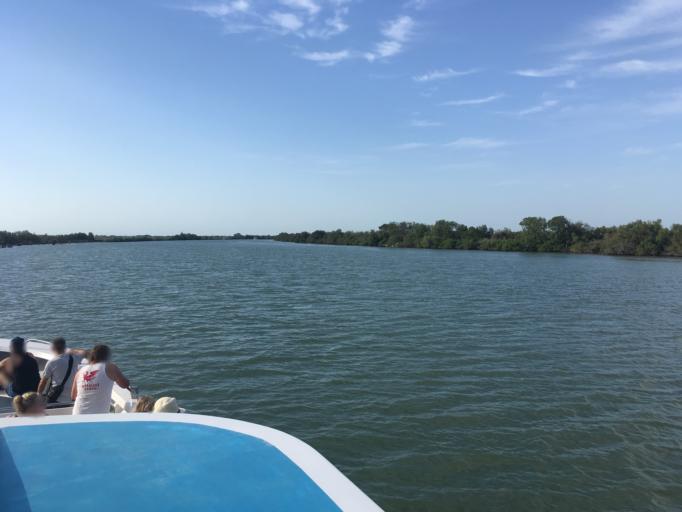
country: FR
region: Provence-Alpes-Cote d'Azur
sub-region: Departement des Bouches-du-Rhone
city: Saintes-Maries-de-la-Mer
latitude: 43.4691
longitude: 4.3794
